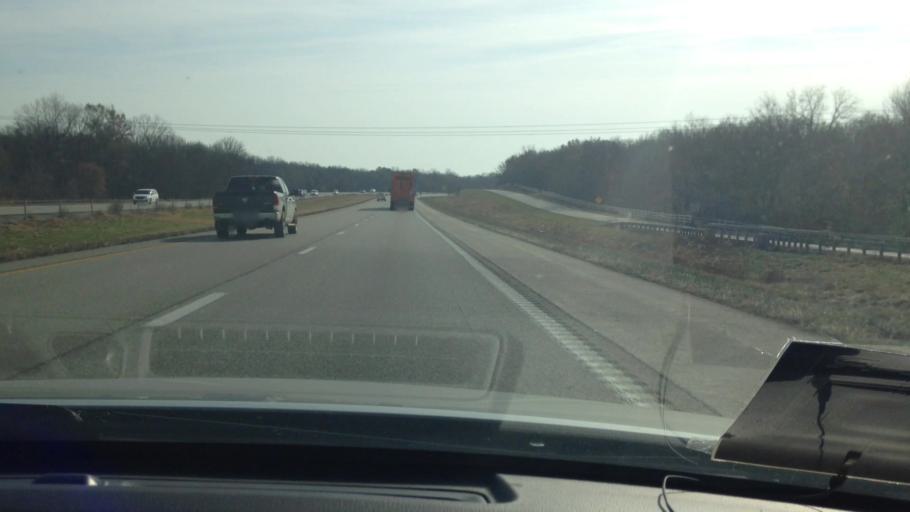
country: US
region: Missouri
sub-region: Cass County
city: Peculiar
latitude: 38.7602
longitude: -94.4867
